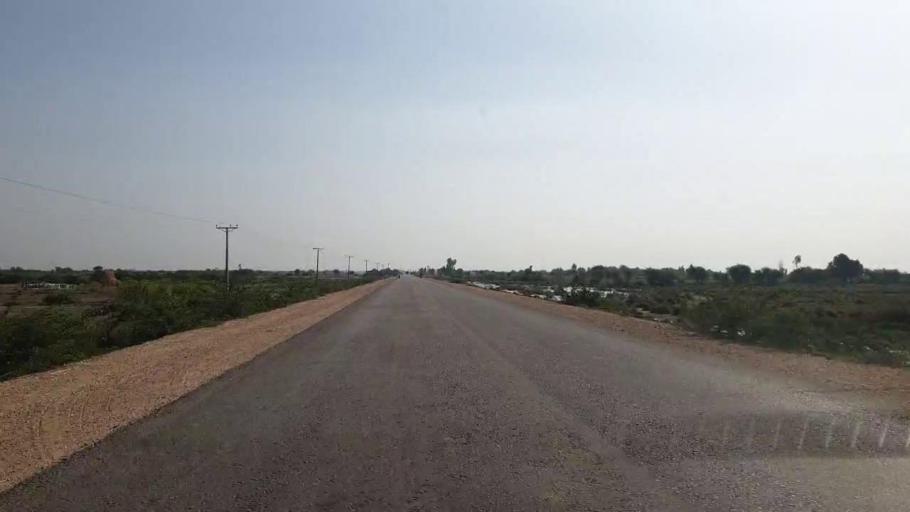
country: PK
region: Sindh
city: Kadhan
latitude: 24.6385
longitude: 69.0674
